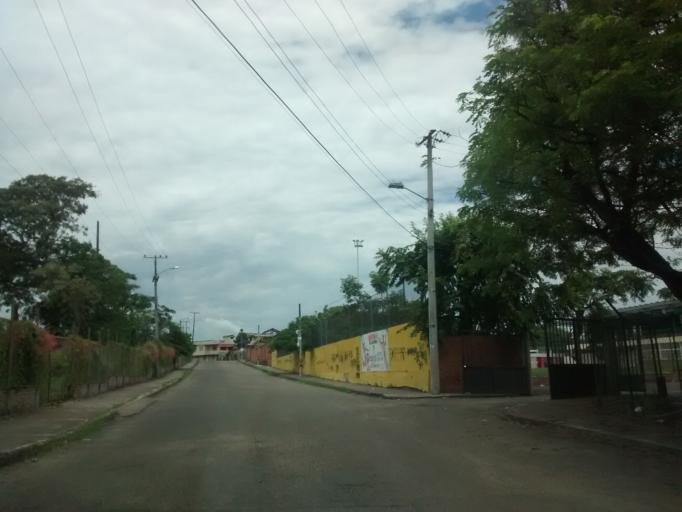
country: CO
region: Cundinamarca
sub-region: Girardot
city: Girardot City
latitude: 4.3056
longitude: -74.8105
